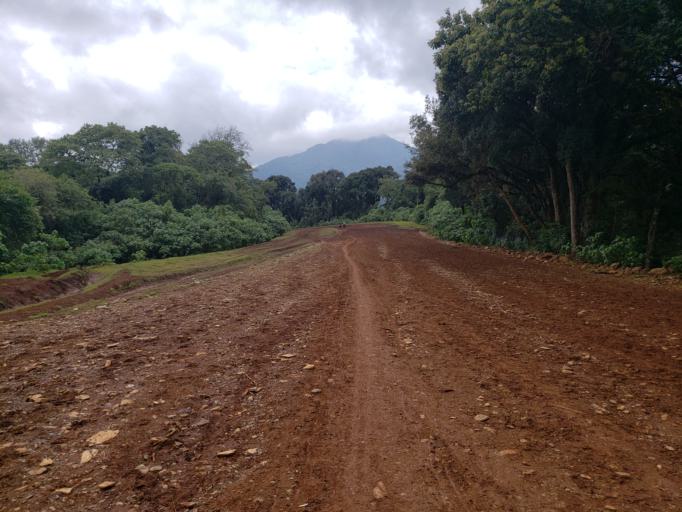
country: ET
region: Oromiya
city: Dodola
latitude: 6.6141
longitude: 39.4196
